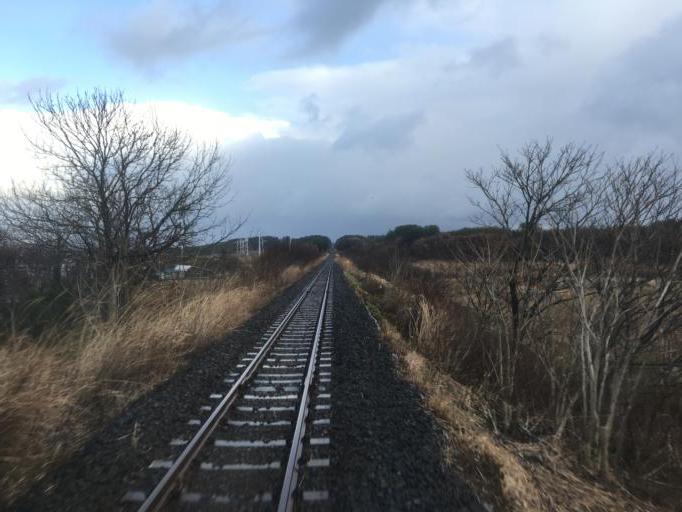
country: JP
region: Aomori
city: Misawa
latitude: 40.9179
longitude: 141.1926
